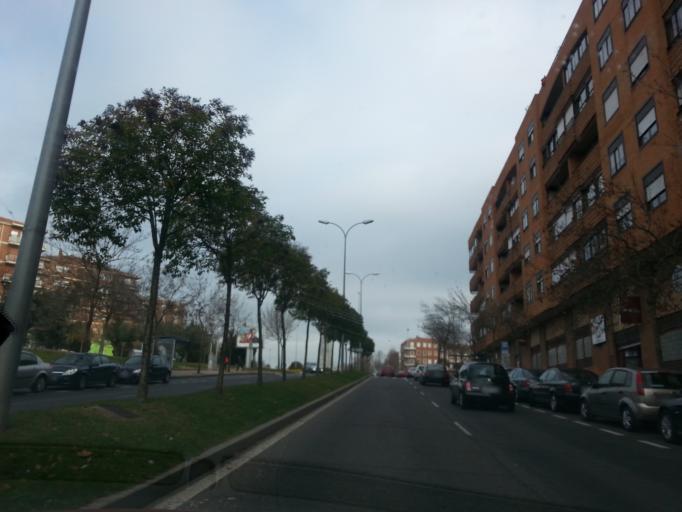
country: ES
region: Castille and Leon
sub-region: Provincia de Salamanca
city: Salamanca
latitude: 40.9724
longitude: -5.6729
